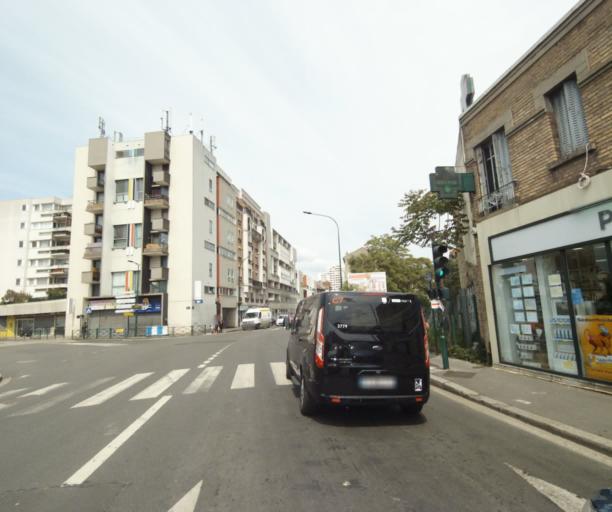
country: FR
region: Ile-de-France
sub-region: Departement des Hauts-de-Seine
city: Bois-Colombes
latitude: 48.9293
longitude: 2.2683
